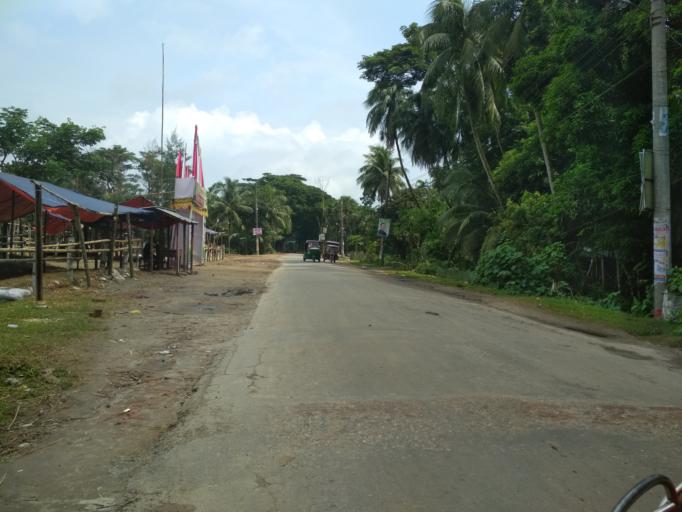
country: BD
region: Chittagong
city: Lakshmipur
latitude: 22.9487
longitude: 90.8086
